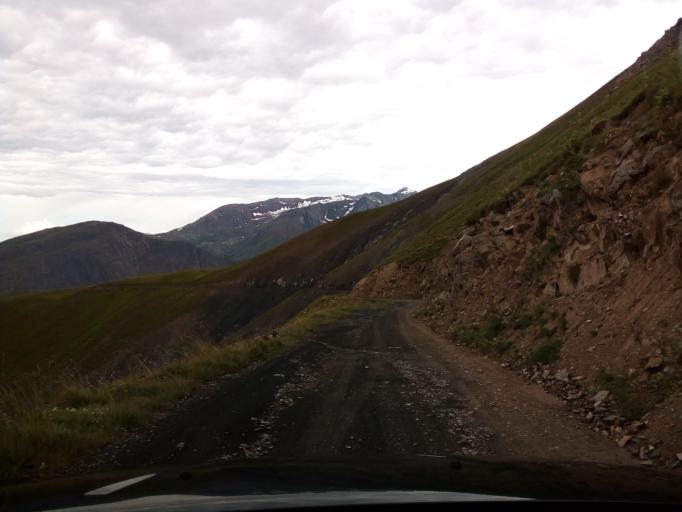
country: FR
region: Rhone-Alpes
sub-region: Departement de l'Isere
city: Mont-de-Lans
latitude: 45.0505
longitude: 6.1929
